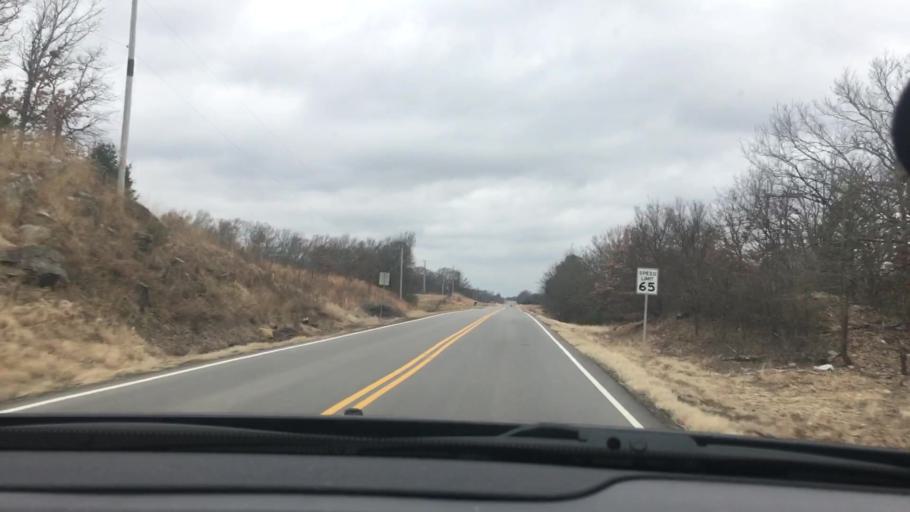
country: US
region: Oklahoma
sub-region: Atoka County
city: Atoka
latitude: 34.3749
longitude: -96.1509
